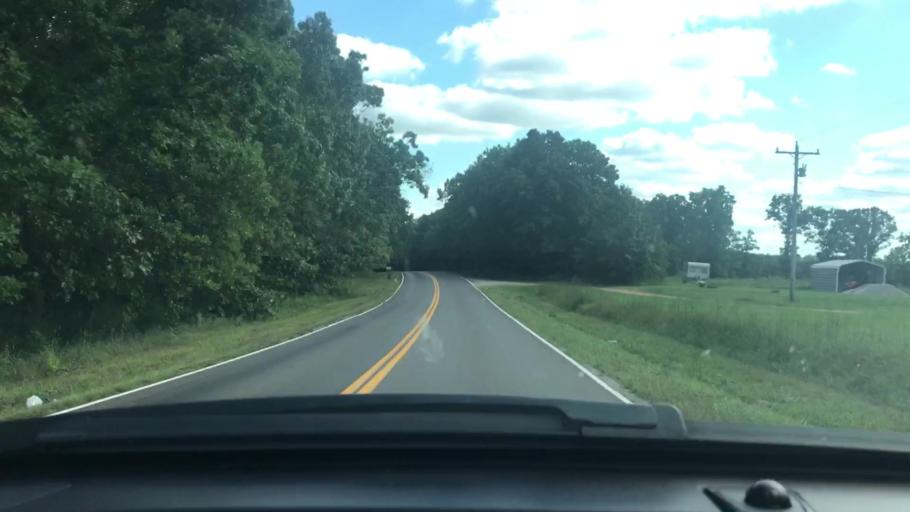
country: US
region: Missouri
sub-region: Wright County
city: Hartville
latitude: 37.3560
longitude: -92.3416
